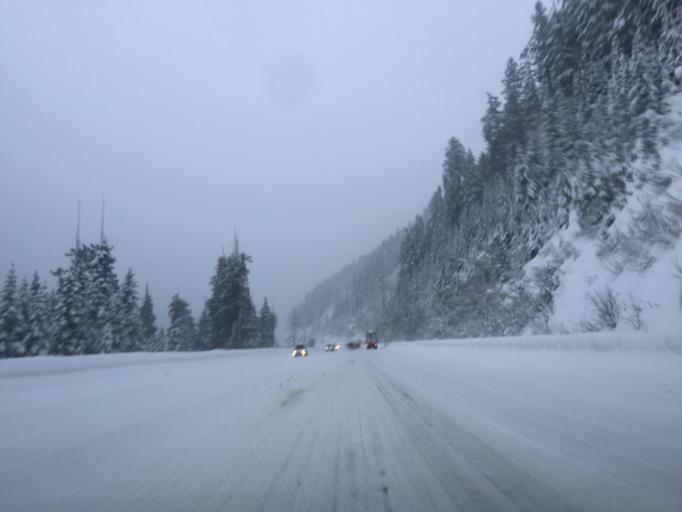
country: US
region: Washington
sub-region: Chelan County
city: Leavenworth
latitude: 47.7352
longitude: -121.1310
